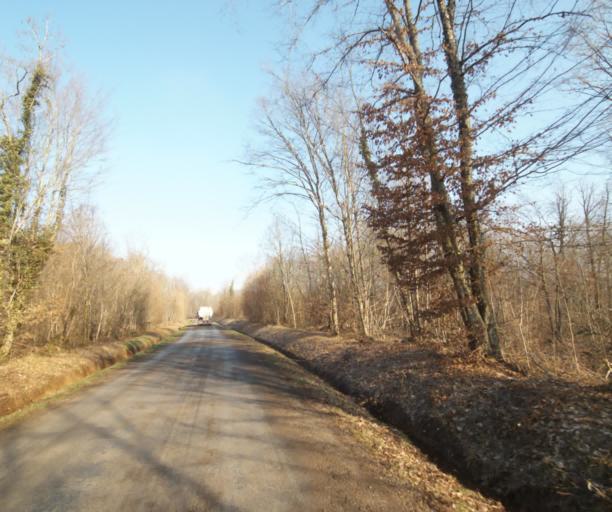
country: FR
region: Champagne-Ardenne
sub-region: Departement de la Haute-Marne
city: Wassy
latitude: 48.5127
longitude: 4.9674
